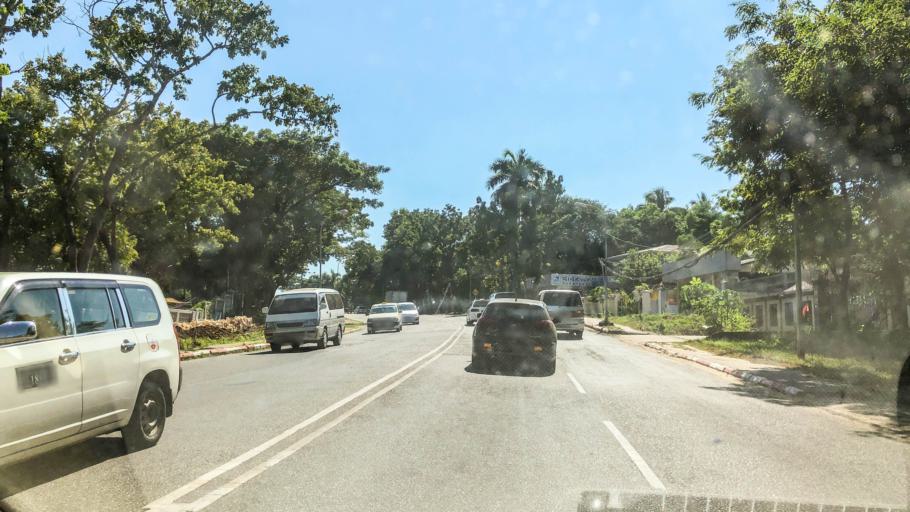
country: MM
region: Yangon
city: Yangon
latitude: 16.8915
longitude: 96.1317
